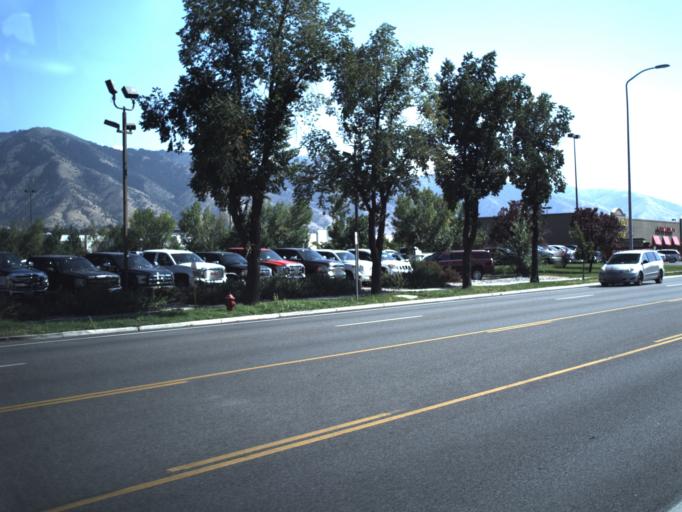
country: US
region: Utah
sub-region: Cache County
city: Logan
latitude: 41.7534
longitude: -111.8345
